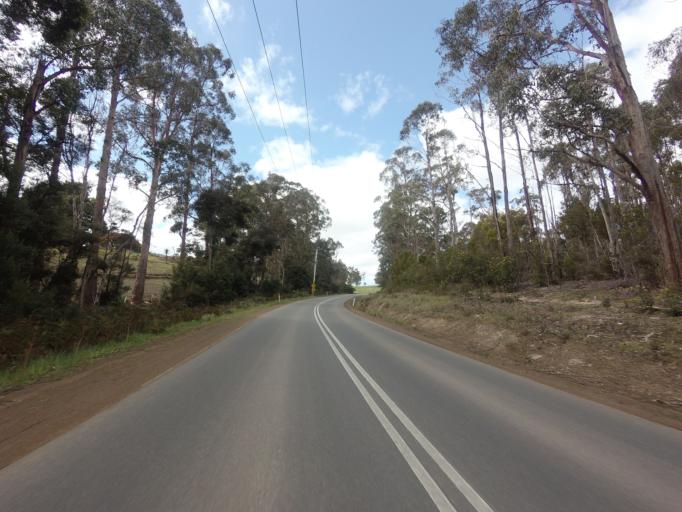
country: AU
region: Tasmania
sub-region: Huon Valley
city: Geeveston
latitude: -43.3236
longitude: 146.9823
